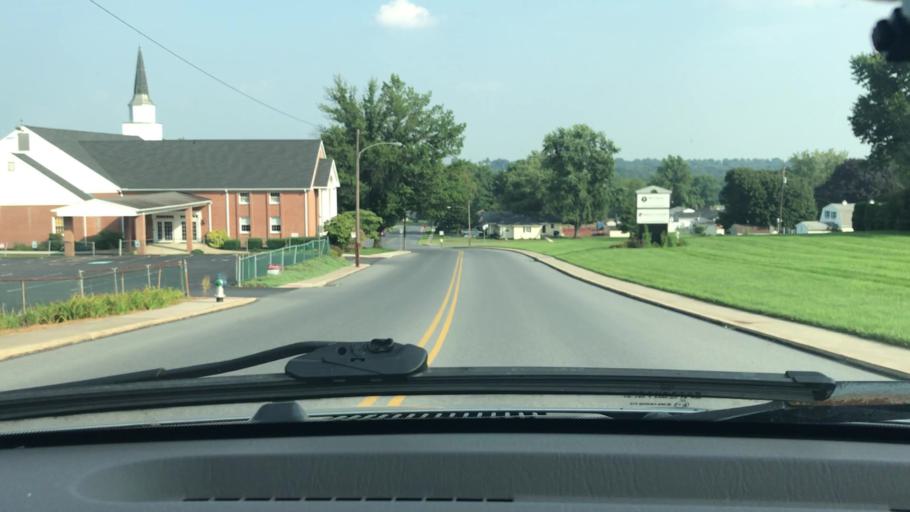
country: US
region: Pennsylvania
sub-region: Lancaster County
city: Elizabethtown
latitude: 40.1644
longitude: -76.6067
